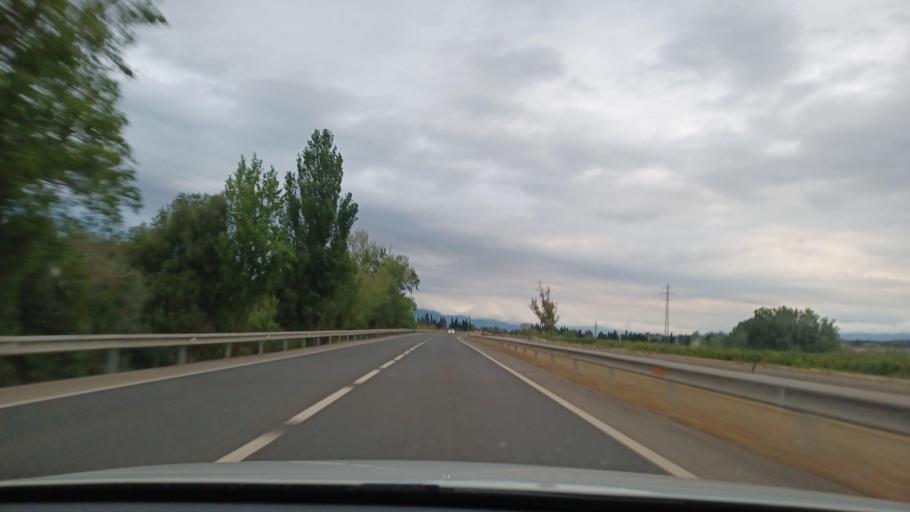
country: ES
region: Catalonia
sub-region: Provincia de Tarragona
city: Masdenverge
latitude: 40.7615
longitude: 0.5342
